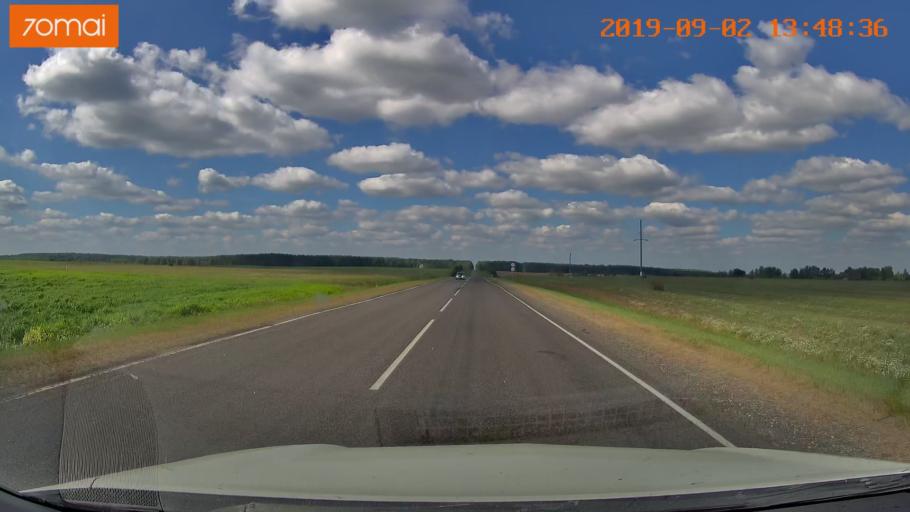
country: BY
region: Mogilev
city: Cherykaw
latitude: 53.6265
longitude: 31.2948
